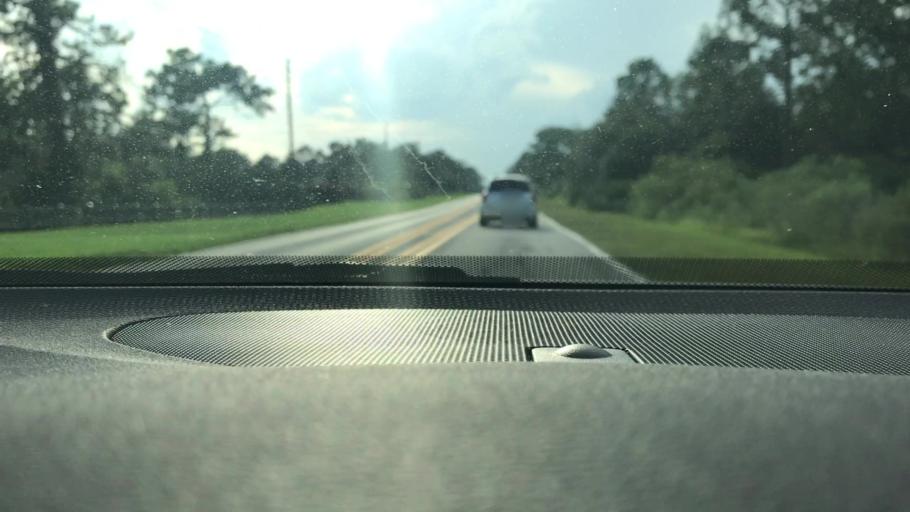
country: US
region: Florida
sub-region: Volusia County
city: Lake Helen
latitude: 28.9847
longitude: -81.2575
